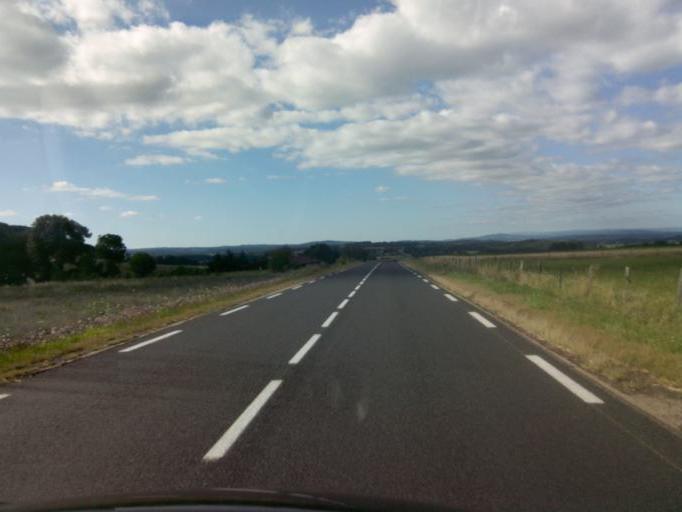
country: FR
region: Auvergne
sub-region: Departement de la Haute-Loire
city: Saint-Paulien
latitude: 45.1789
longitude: 3.8265
